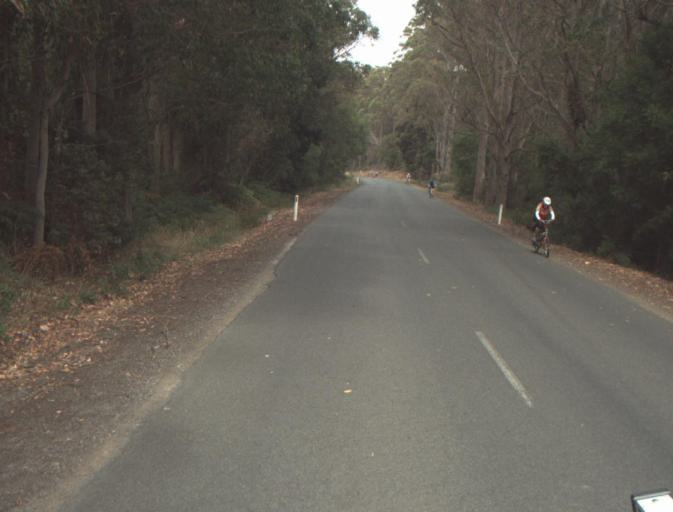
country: AU
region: Tasmania
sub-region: Launceston
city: Mayfield
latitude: -41.2109
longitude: 147.2131
